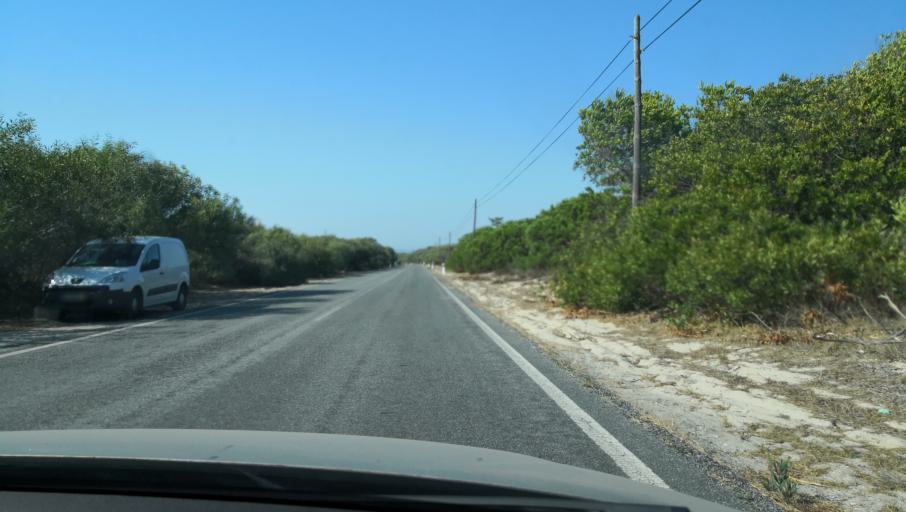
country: PT
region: Setubal
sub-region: Setubal
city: Setubal
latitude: 38.4064
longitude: -8.8099
